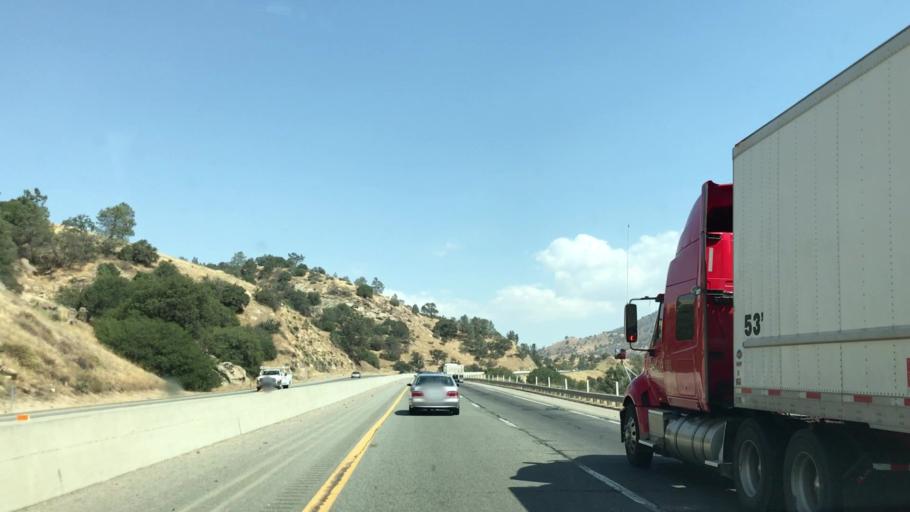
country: US
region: California
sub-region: Kern County
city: Bear Valley Springs
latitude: 35.2197
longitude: -118.5559
